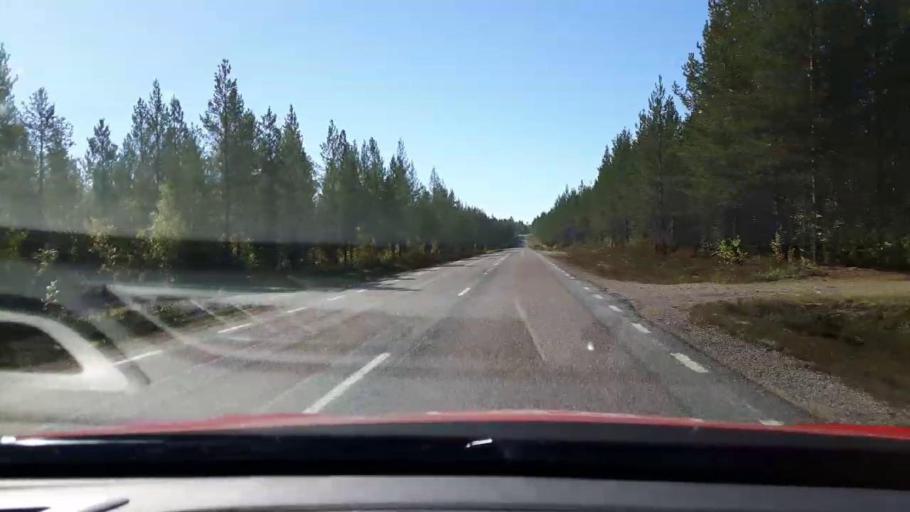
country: SE
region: Jaemtland
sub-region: Harjedalens Kommun
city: Sveg
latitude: 62.1359
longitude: 14.1699
